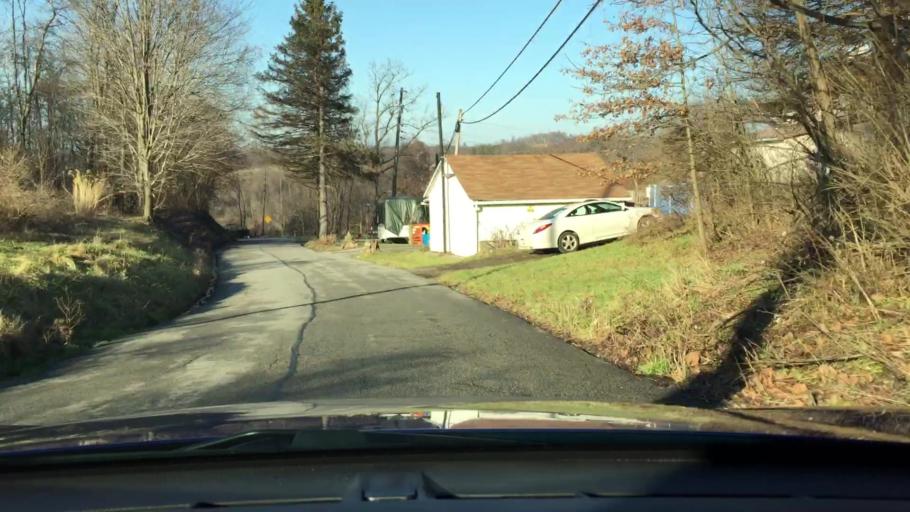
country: US
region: Pennsylvania
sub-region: Westmoreland County
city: Delmont
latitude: 40.4151
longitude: -79.6312
